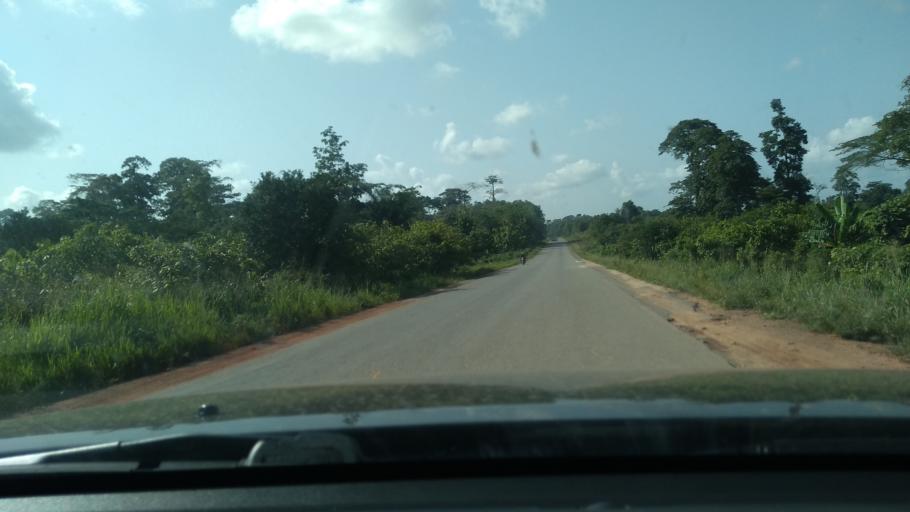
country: CI
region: Bas-Sassandra
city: Soubre
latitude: 5.7396
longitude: -6.6256
